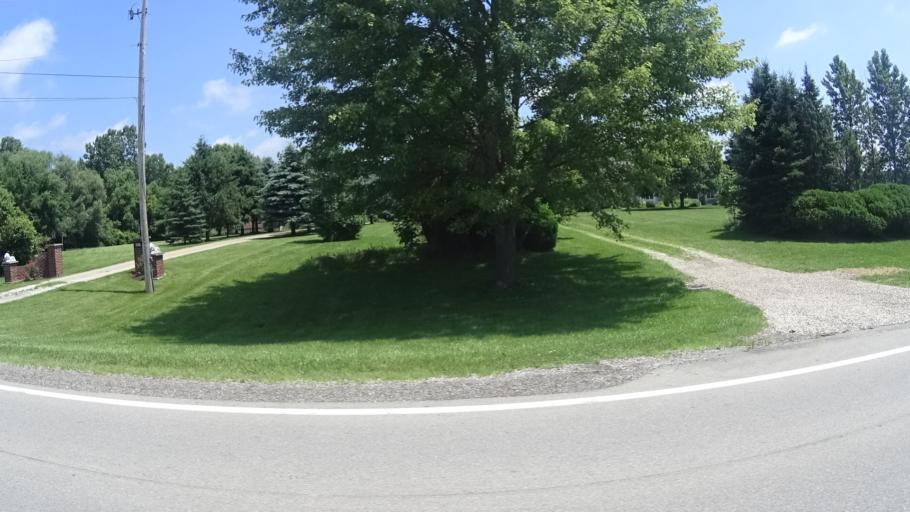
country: US
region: Ohio
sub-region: Lorain County
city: Vermilion
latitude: 41.3554
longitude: -82.3594
